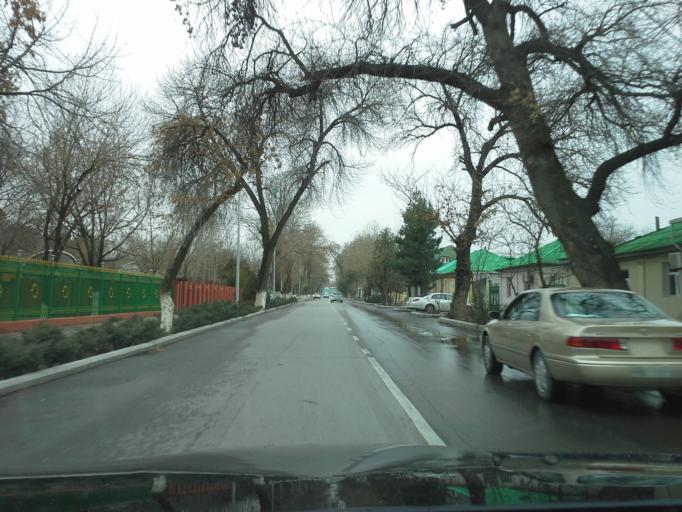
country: TM
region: Ahal
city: Ashgabat
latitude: 37.9532
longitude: 58.3642
